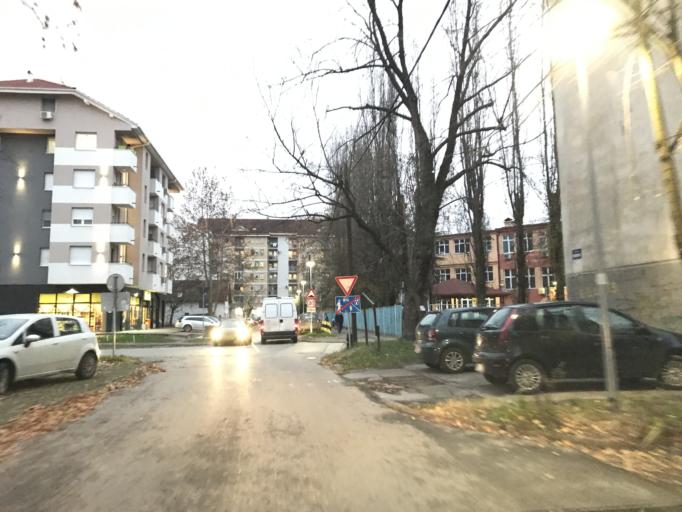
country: RS
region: Autonomna Pokrajina Vojvodina
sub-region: Juznobacki Okrug
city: Novi Sad
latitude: 45.2664
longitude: 19.8133
